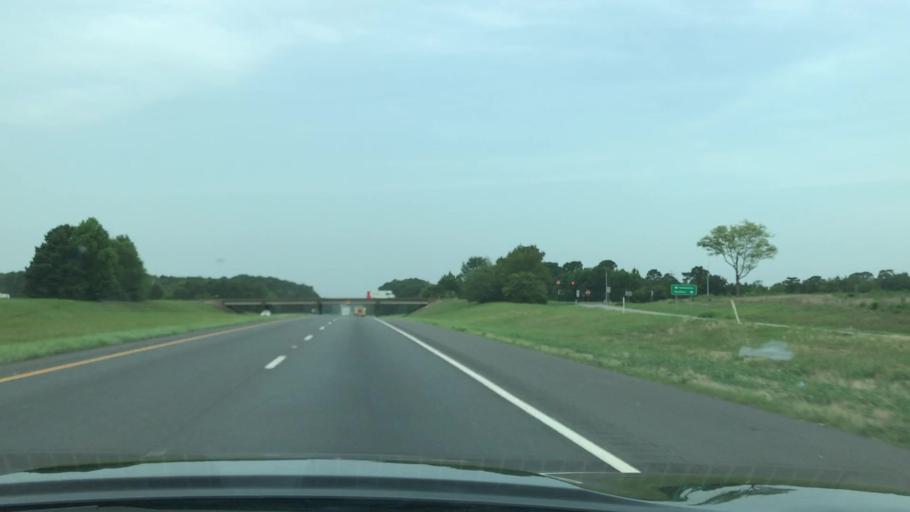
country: US
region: Texas
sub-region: Harrison County
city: Marshall
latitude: 32.4893
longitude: -94.4064
